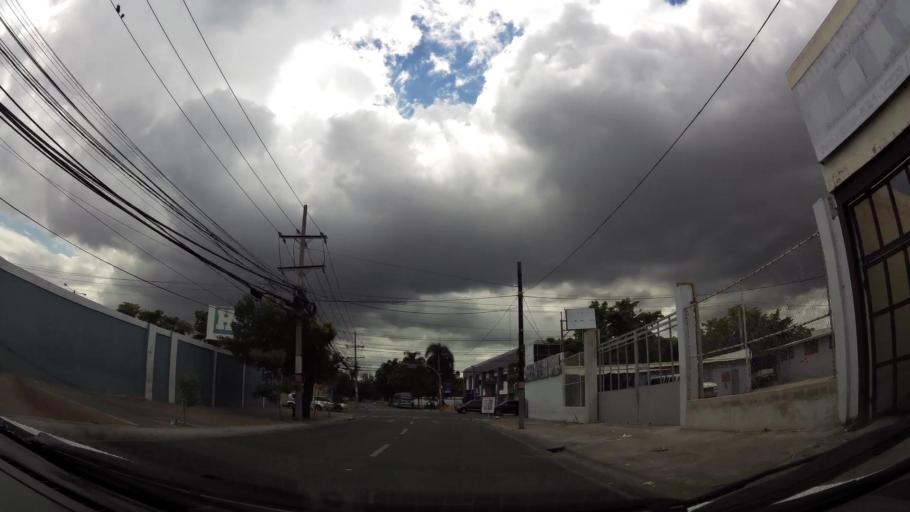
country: DO
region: Nacional
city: La Agustina
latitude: 18.4852
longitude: -69.9206
